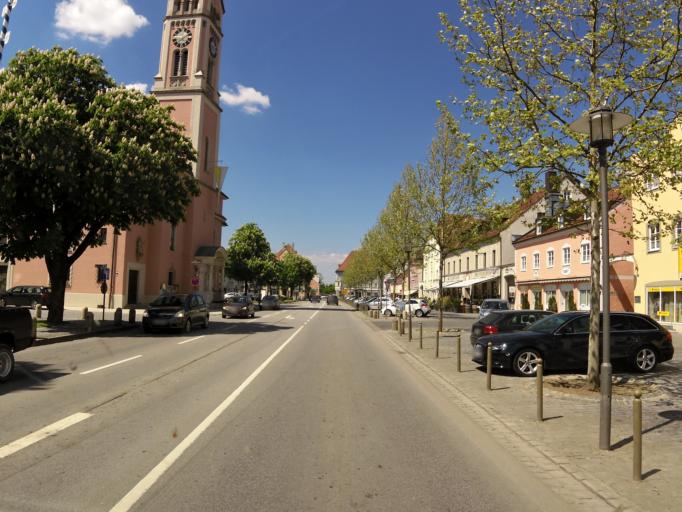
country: DE
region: Bavaria
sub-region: Lower Bavaria
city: Plattling
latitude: 48.7768
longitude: 12.8734
